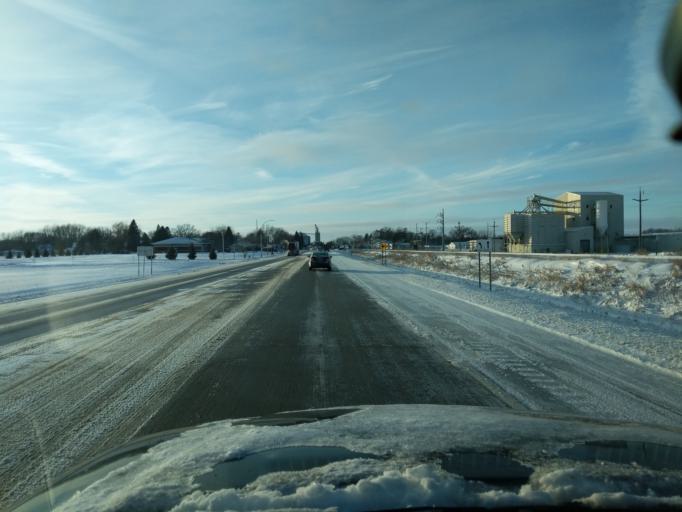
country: US
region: Minnesota
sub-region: Renville County
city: Olivia
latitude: 44.7759
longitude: -94.9724
